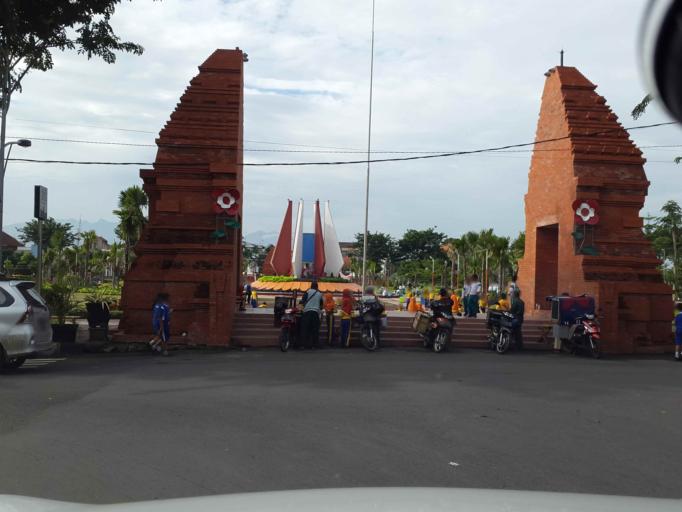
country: ID
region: East Java
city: Mojokerto
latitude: -7.4623
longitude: 112.4320
